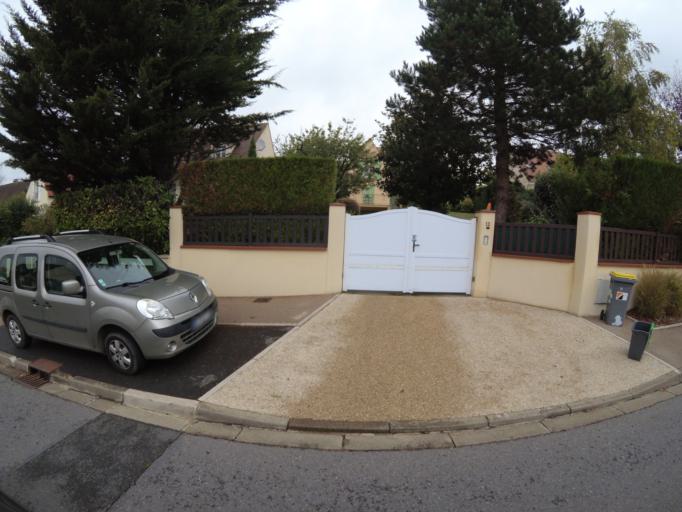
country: FR
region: Ile-de-France
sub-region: Departement de Seine-et-Marne
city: Gouvernes
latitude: 48.8475
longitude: 2.6907
